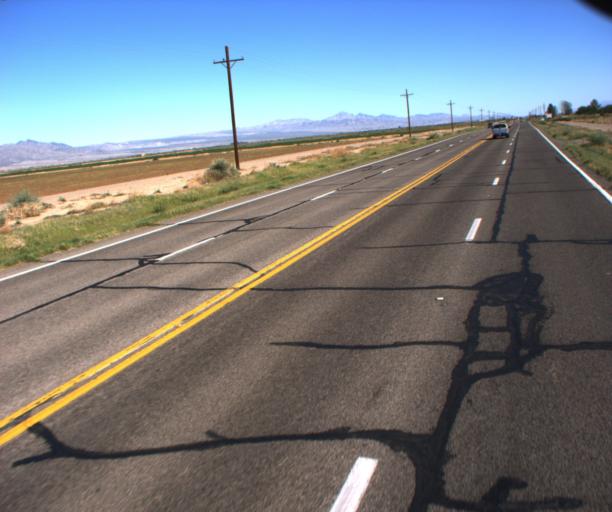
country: US
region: Arizona
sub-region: Mohave County
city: Mohave Valley
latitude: 34.9273
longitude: -114.5978
